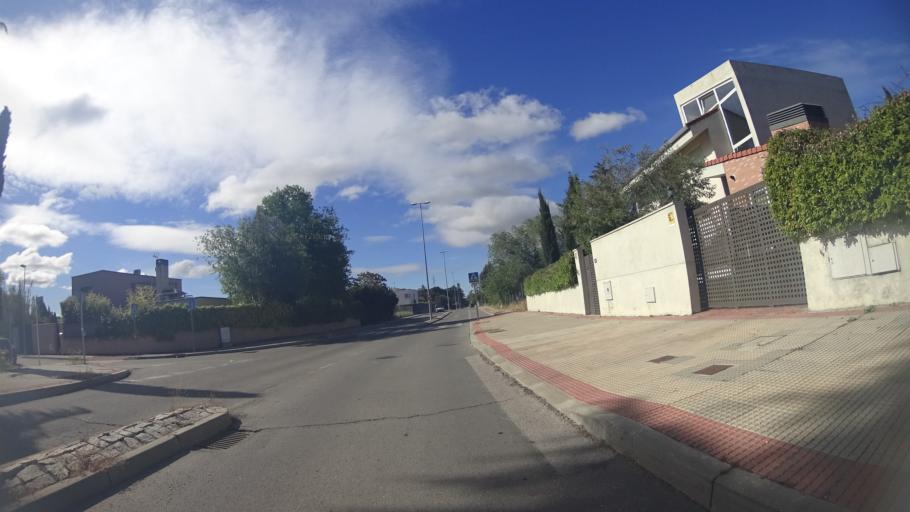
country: ES
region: Madrid
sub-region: Provincia de Madrid
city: Villanueva del Pardillo
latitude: 40.4885
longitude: -3.9396
